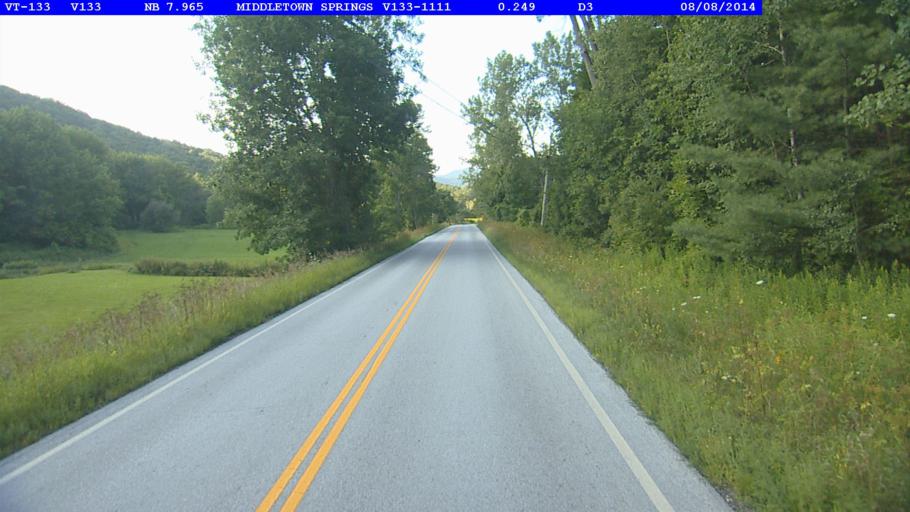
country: US
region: Vermont
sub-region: Rutland County
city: Poultney
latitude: 43.4392
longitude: -73.1120
